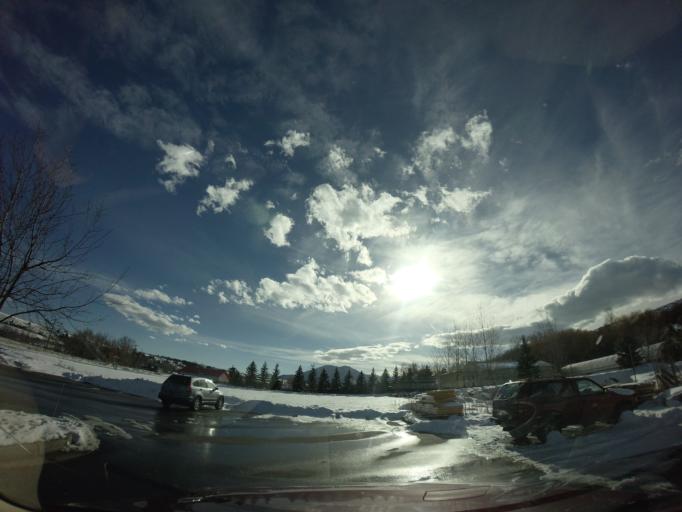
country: US
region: Montana
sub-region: Carbon County
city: Red Lodge
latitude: 45.2019
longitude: -109.2466
